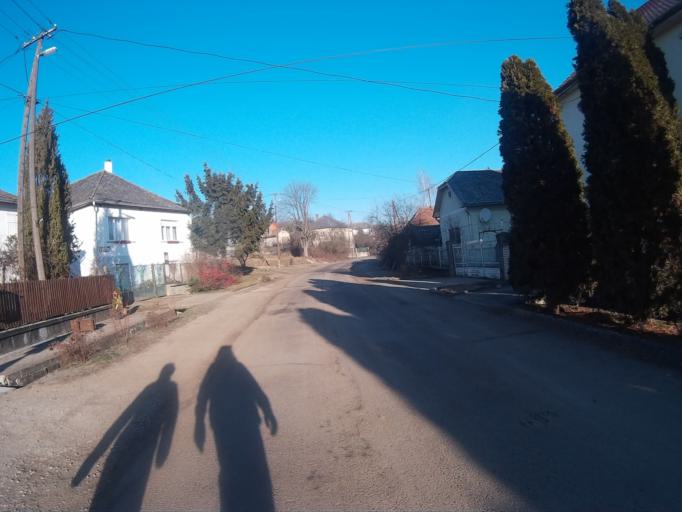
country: HU
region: Borsod-Abauj-Zemplen
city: Putnok
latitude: 48.3727
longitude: 20.4272
